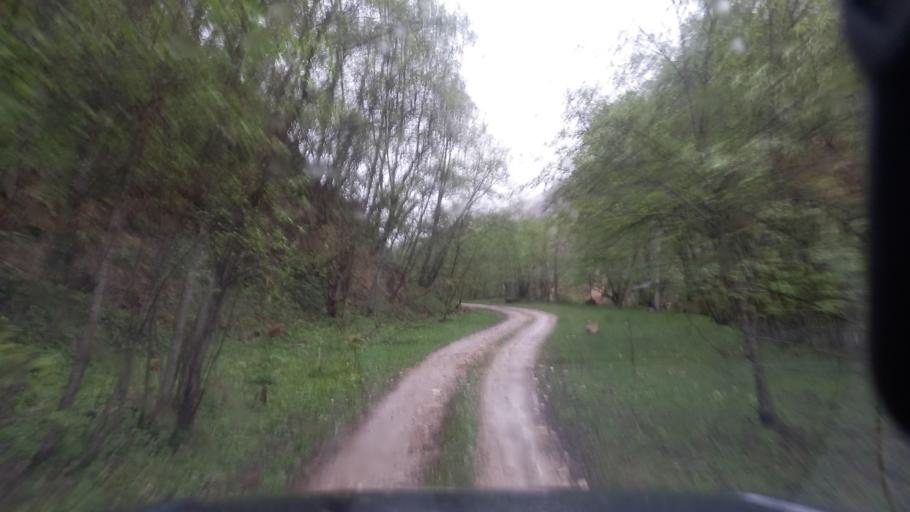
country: RU
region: Kabardino-Balkariya
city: Bylym
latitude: 43.5998
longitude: 42.9265
